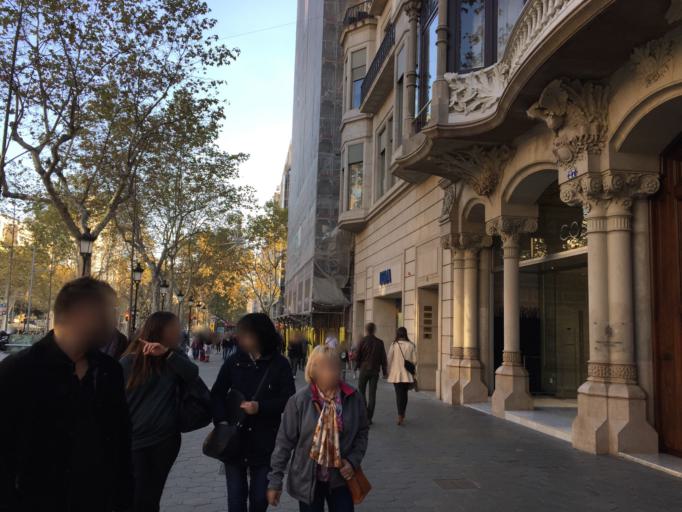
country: ES
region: Catalonia
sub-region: Provincia de Barcelona
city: Eixample
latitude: 41.3908
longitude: 2.1662
